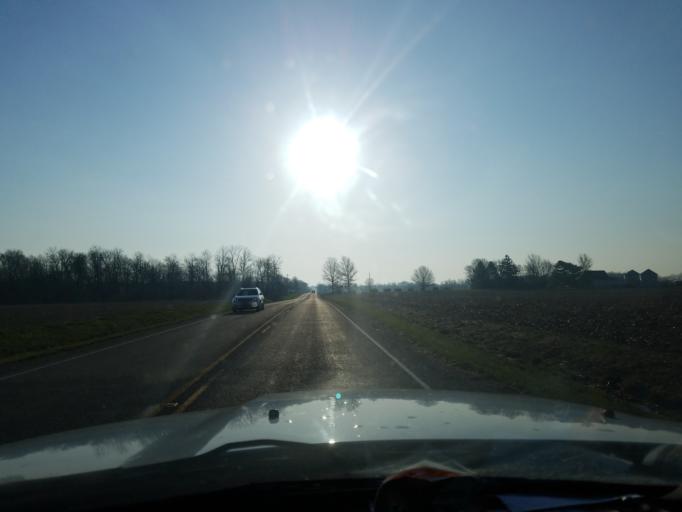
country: US
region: Indiana
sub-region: Vigo County
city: Seelyville
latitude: 39.3903
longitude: -87.2568
